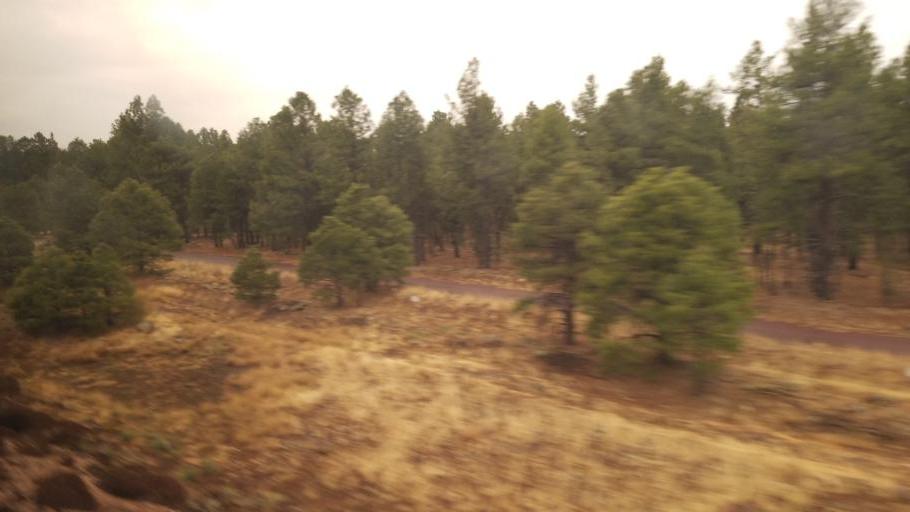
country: US
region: Arizona
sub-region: Coconino County
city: Parks
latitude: 35.2430
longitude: -111.8687
